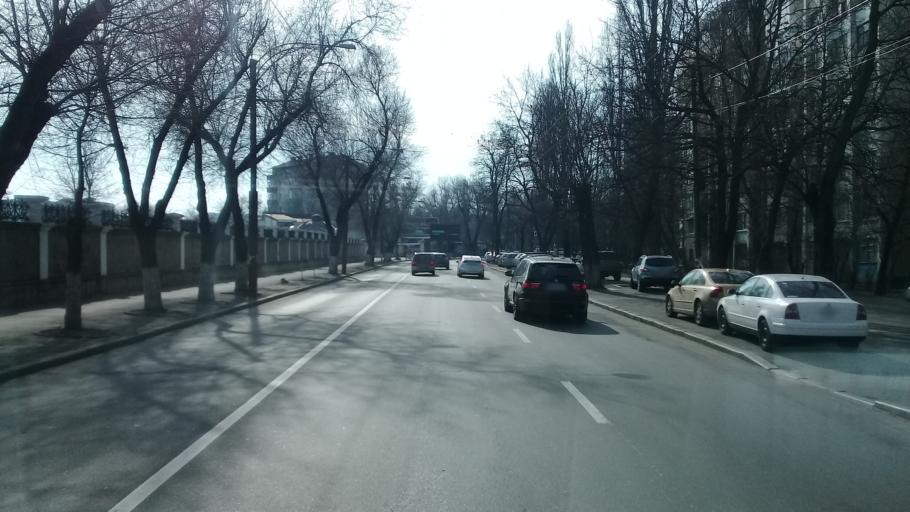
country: MD
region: Chisinau
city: Chisinau
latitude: 47.0103
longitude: 28.8280
